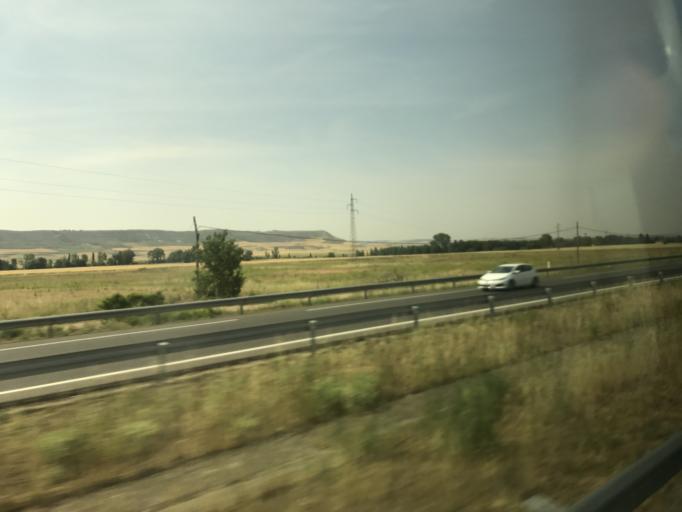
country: ES
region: Castille and Leon
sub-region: Provincia de Palencia
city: Palenzuela
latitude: 42.1302
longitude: -4.1280
